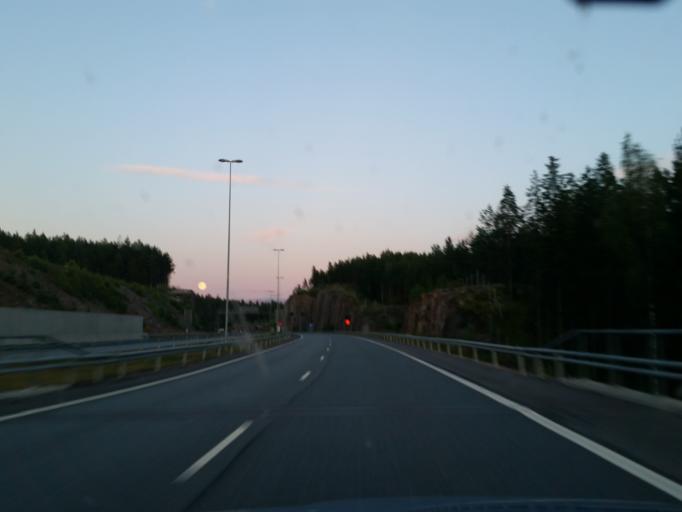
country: FI
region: Uusimaa
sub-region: Helsinki
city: Saukkola
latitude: 60.3174
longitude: 23.9693
